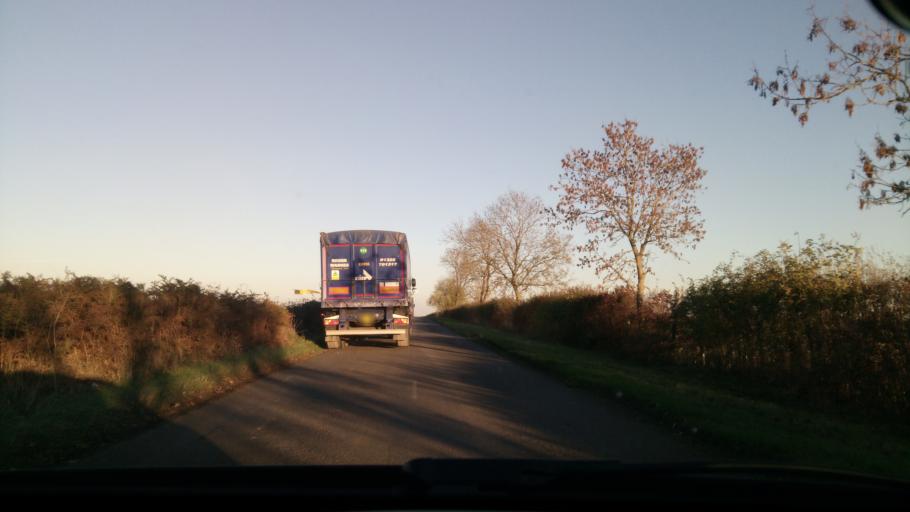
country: GB
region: England
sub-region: Peterborough
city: Wittering
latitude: 52.6265
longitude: -0.4346
